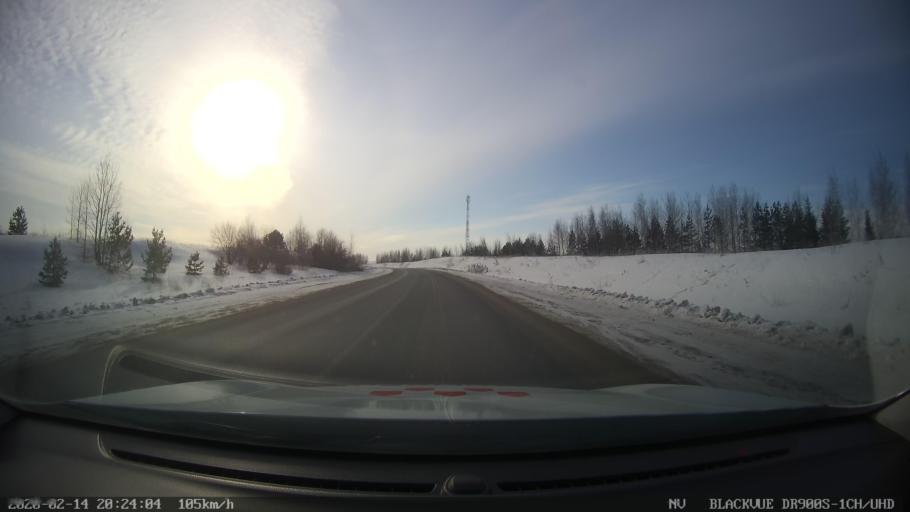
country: RU
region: Tatarstan
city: Verkhniy Uslon
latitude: 55.5183
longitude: 48.9672
